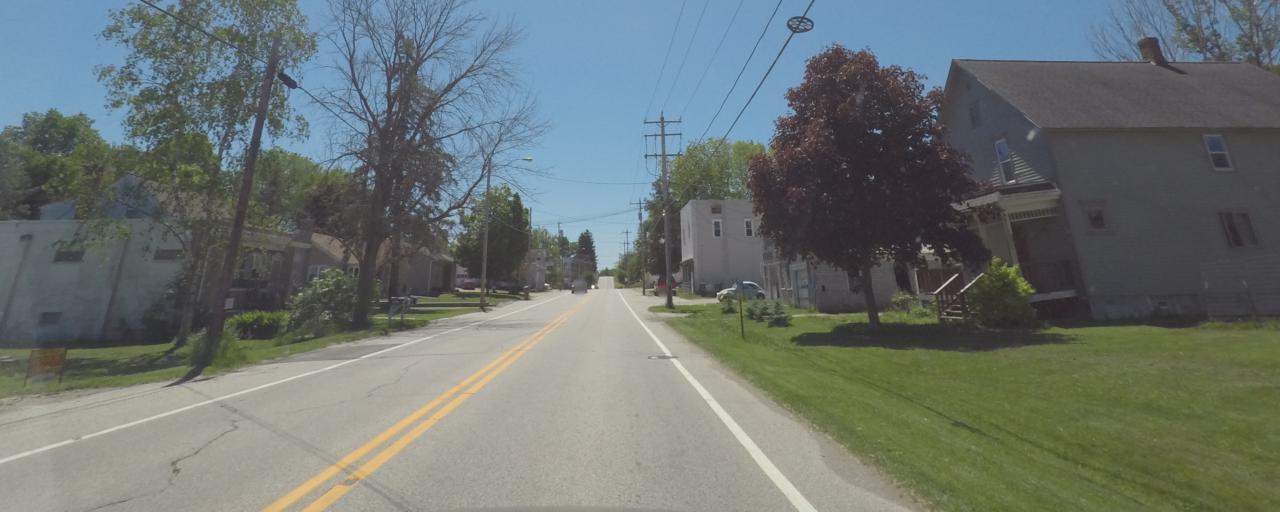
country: US
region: Wisconsin
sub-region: Sheboygan County
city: Random Lake
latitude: 43.5927
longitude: -88.0504
